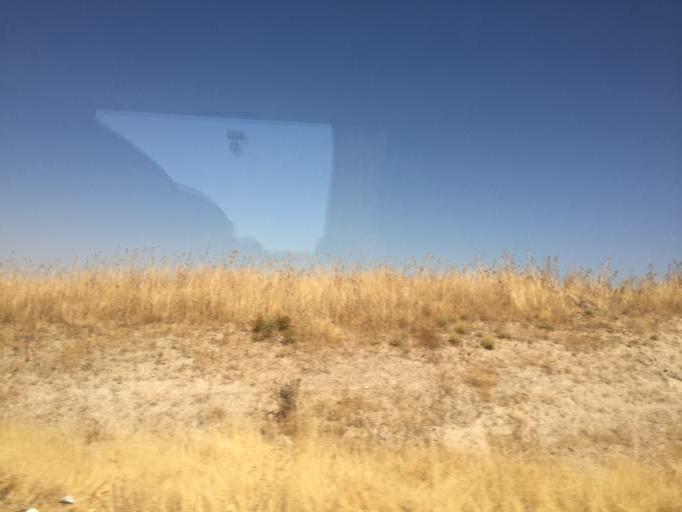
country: TR
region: Diyarbakir
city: Salat
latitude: 37.8589
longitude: 40.8655
